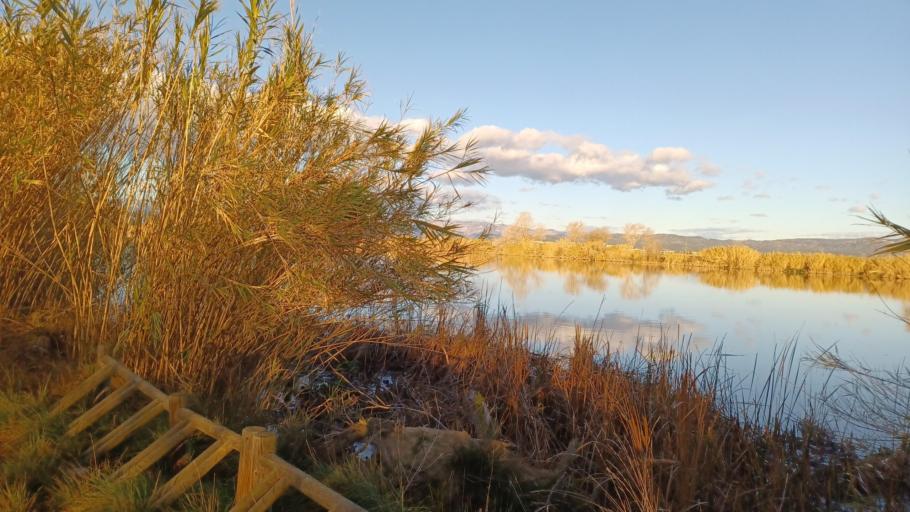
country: ES
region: Catalonia
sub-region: Provincia de Tarragona
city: Deltebre
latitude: 40.7194
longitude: 0.6662
